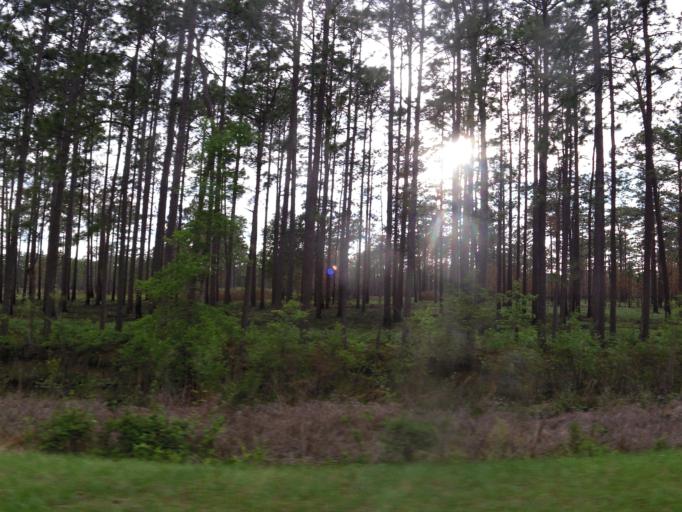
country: US
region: South Carolina
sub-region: Jasper County
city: Hardeeville
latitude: 32.3451
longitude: -81.0924
